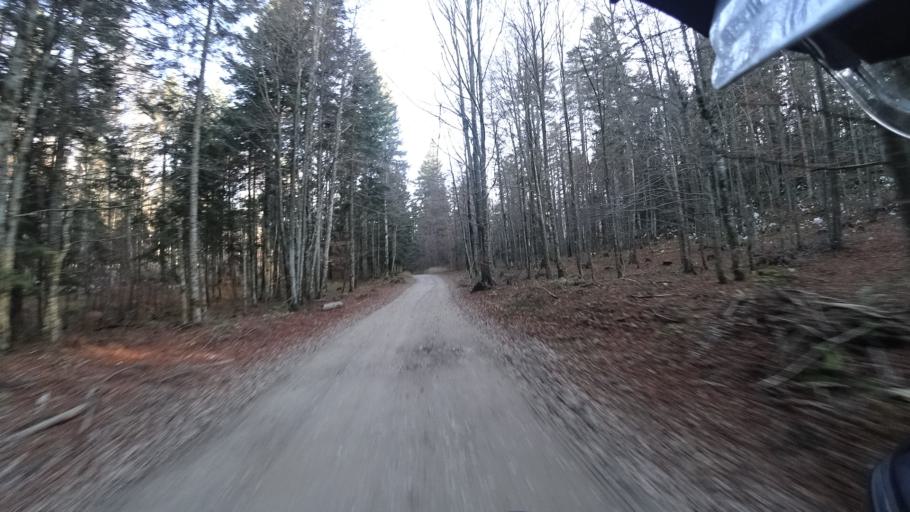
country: HR
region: Primorsko-Goranska
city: Drazice
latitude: 45.4834
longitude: 14.4694
